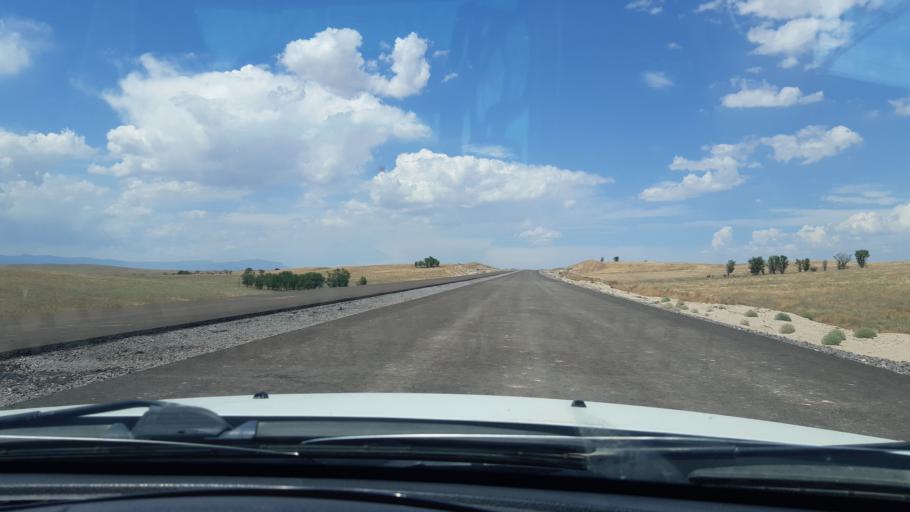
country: KG
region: Chuy
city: Bystrovka
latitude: 43.2981
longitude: 76.1504
